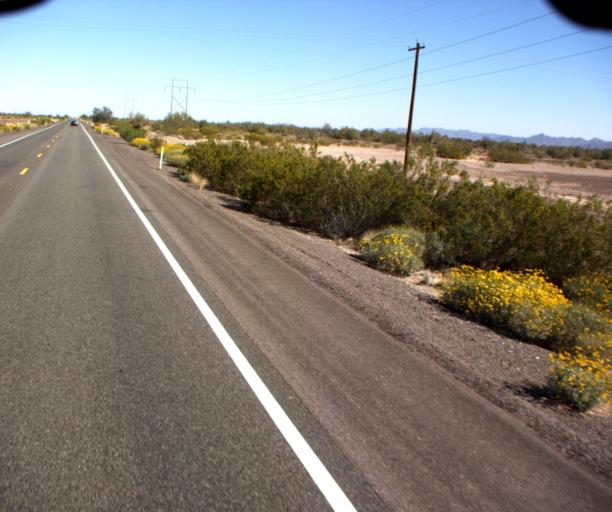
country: US
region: Arizona
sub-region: La Paz County
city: Quartzsite
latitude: 33.5445
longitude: -114.2170
